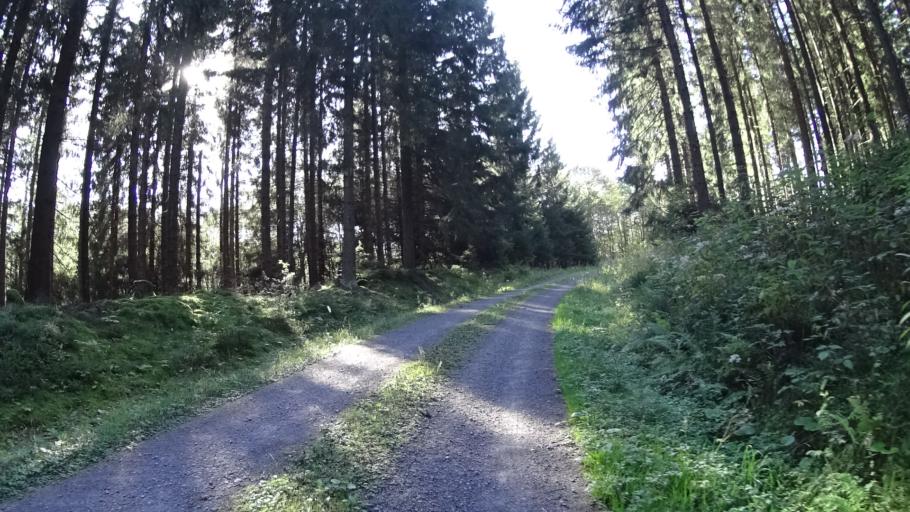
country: DE
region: Thuringia
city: Neuhaus
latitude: 50.6390
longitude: 10.9288
